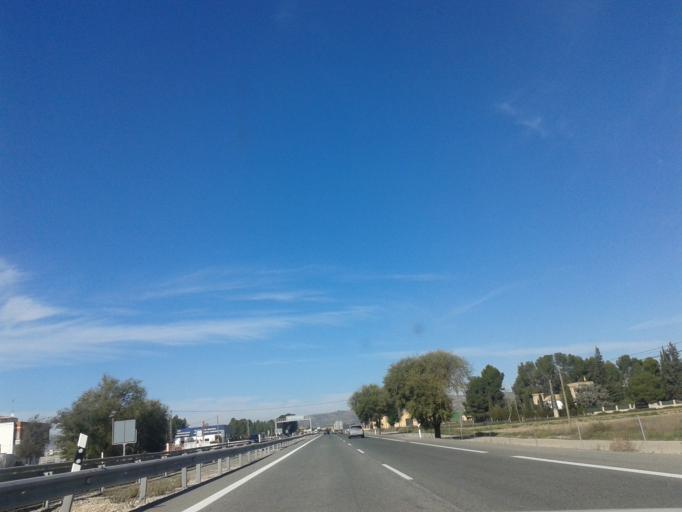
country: ES
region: Valencia
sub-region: Provincia de Alicante
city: Villena
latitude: 38.6531
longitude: -0.8740
